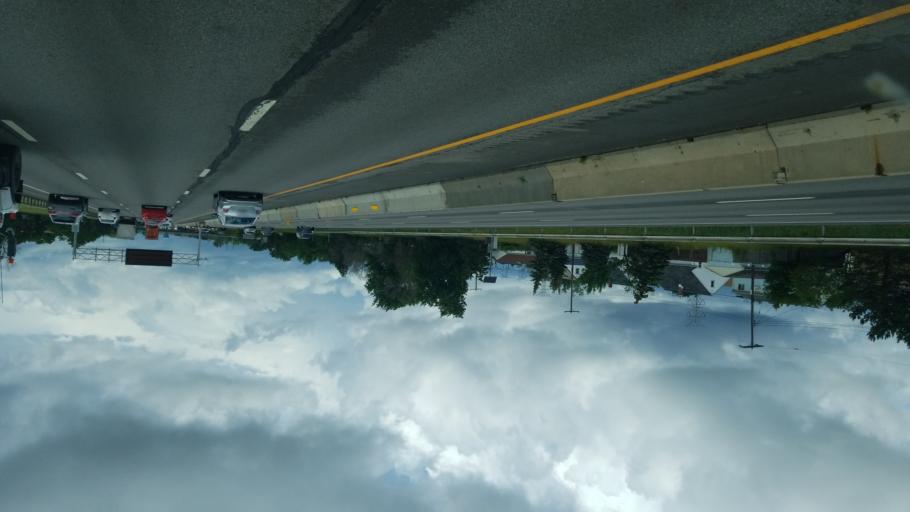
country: US
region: New York
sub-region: Erie County
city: Cheektowaga
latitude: 42.9202
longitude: -78.7662
